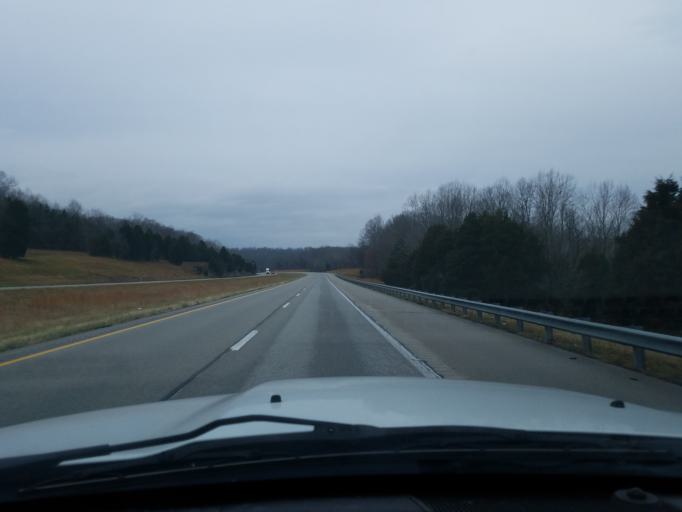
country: US
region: Indiana
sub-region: Crawford County
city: English
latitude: 38.2548
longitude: -86.3015
